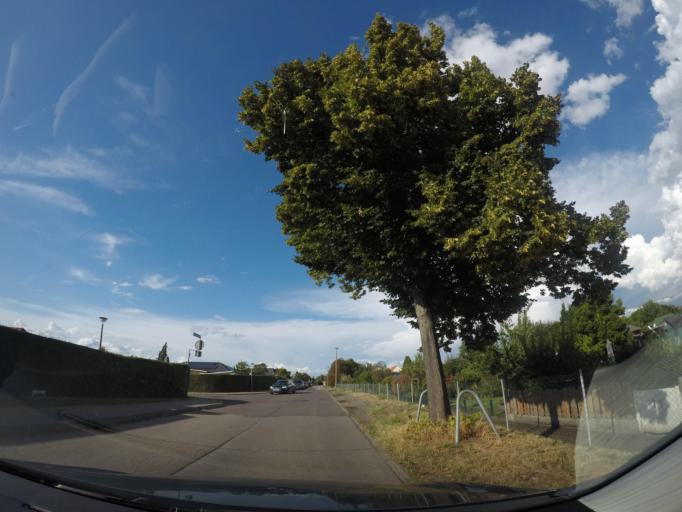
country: DE
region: Saxony-Anhalt
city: Diesdorf
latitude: 52.1341
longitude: 11.5804
